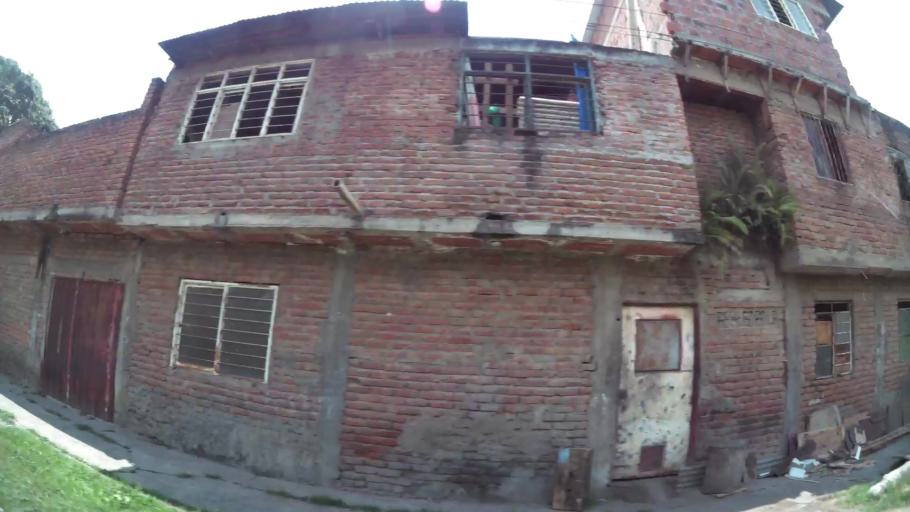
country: CO
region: Valle del Cauca
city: Cali
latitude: 3.4550
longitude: -76.4775
